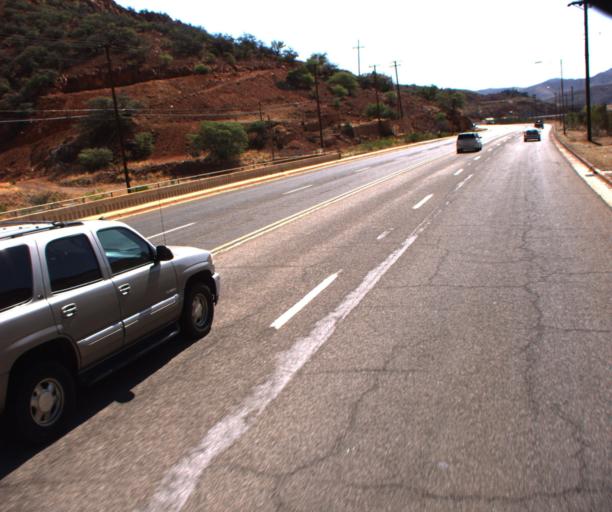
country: US
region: Arizona
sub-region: Cochise County
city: Bisbee
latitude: 31.4371
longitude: -109.9051
